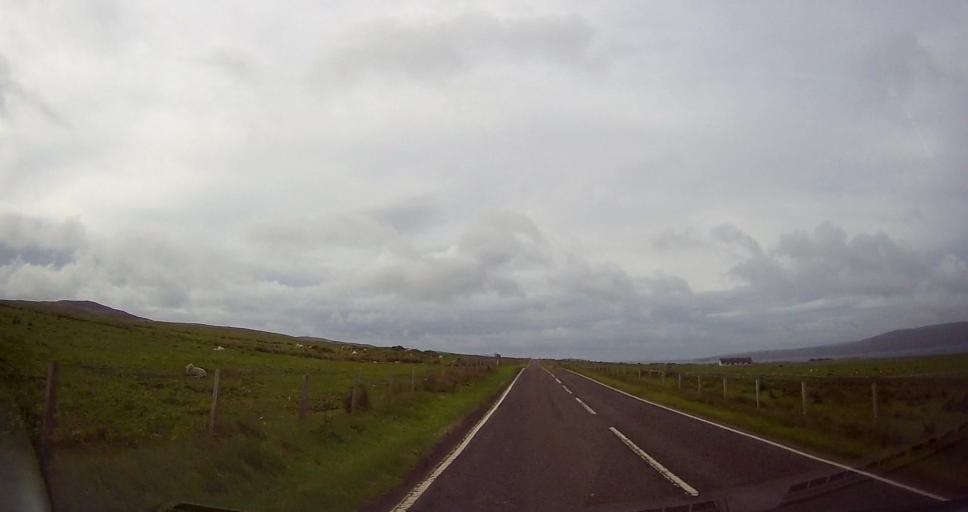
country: GB
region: Scotland
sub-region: Orkney Islands
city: Stromness
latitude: 58.9518
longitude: -3.2176
